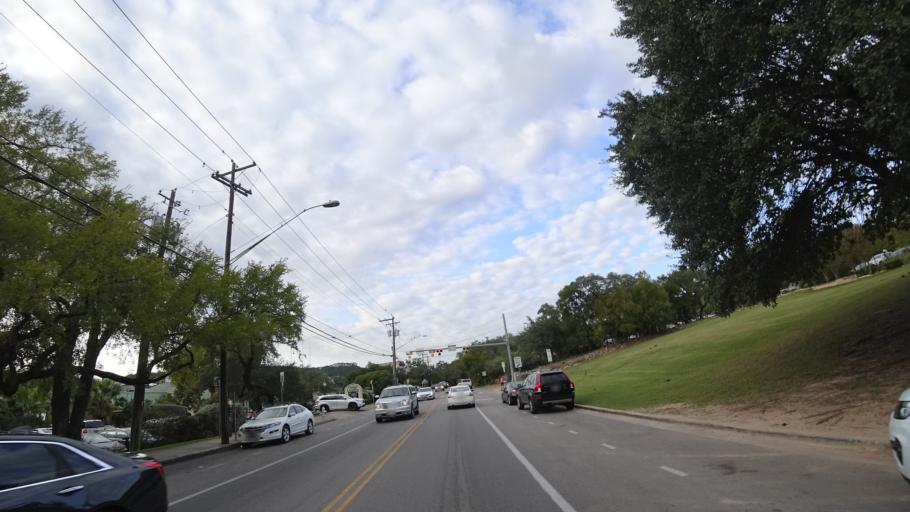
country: US
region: Texas
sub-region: Travis County
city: West Lake Hills
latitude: 30.2946
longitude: -97.7837
